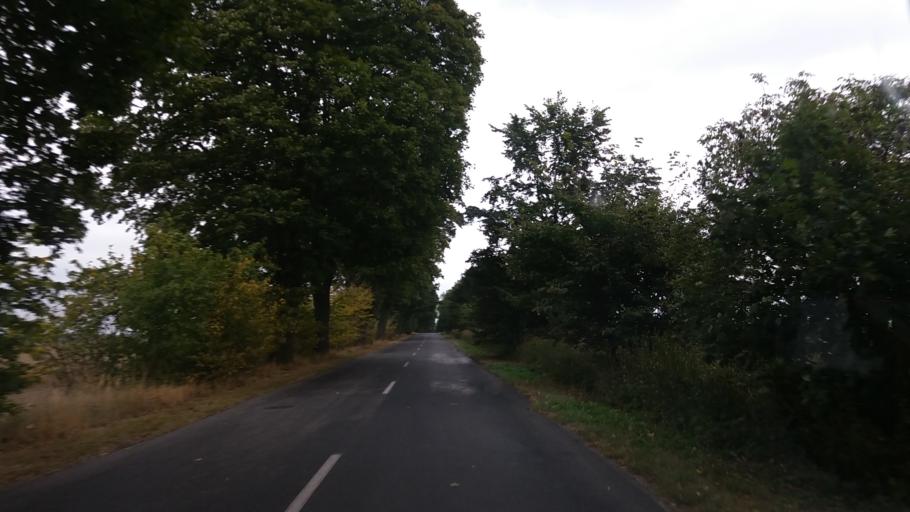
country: PL
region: Lubusz
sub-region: Powiat strzelecko-drezdenecki
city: Strzelce Krajenskie
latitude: 52.9666
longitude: 15.4661
